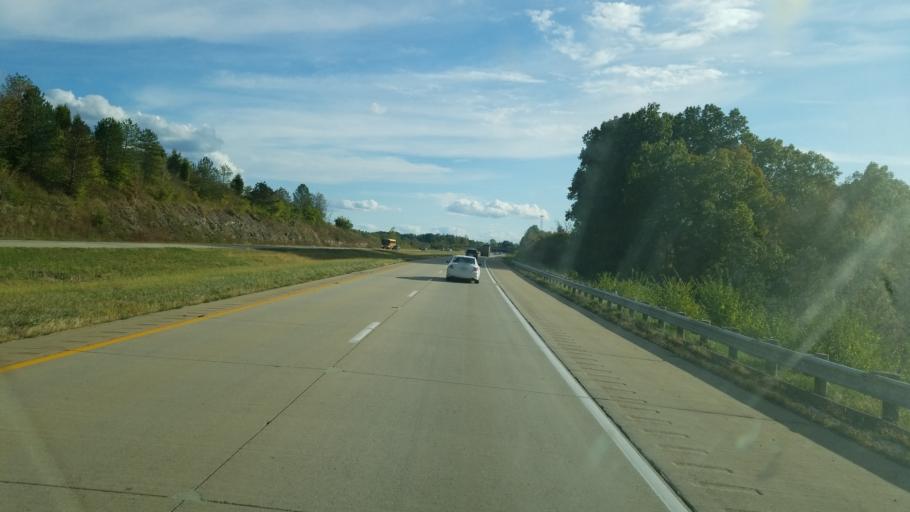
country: US
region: Ohio
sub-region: Washington County
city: Devola
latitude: 39.5513
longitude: -81.4483
